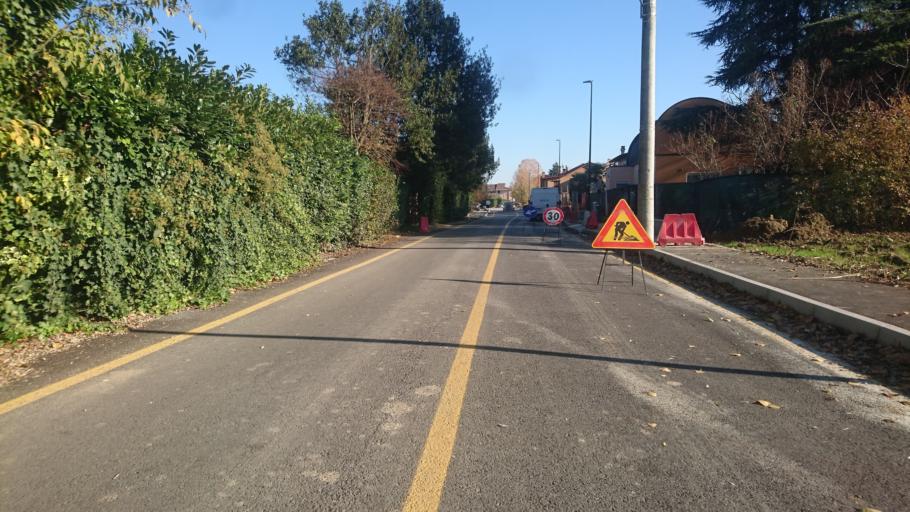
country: IT
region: Veneto
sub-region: Provincia di Padova
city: Caselle
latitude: 45.4045
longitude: 11.8424
